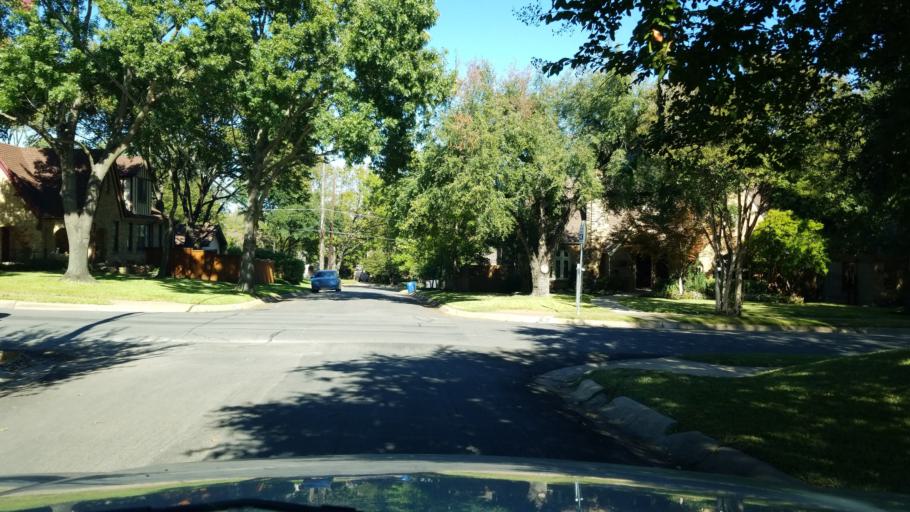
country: US
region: Texas
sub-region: Dallas County
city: Highland Park
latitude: 32.8058
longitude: -96.7431
